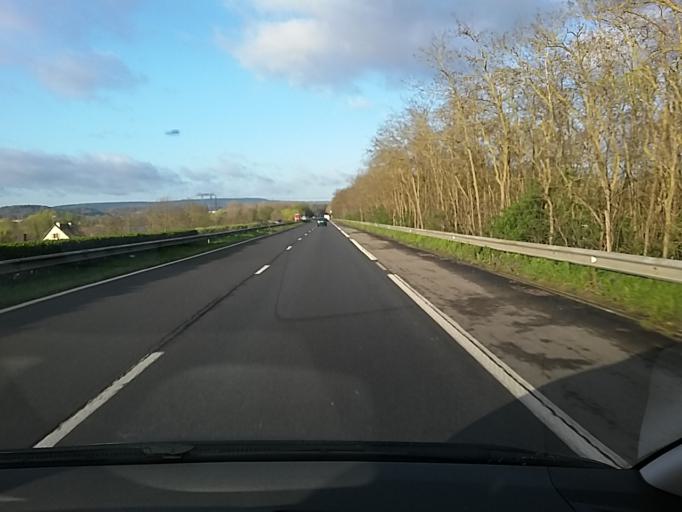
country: FR
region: Picardie
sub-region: Departement de l'Oise
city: Longueil-Sainte-Marie
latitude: 49.3342
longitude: 2.7250
